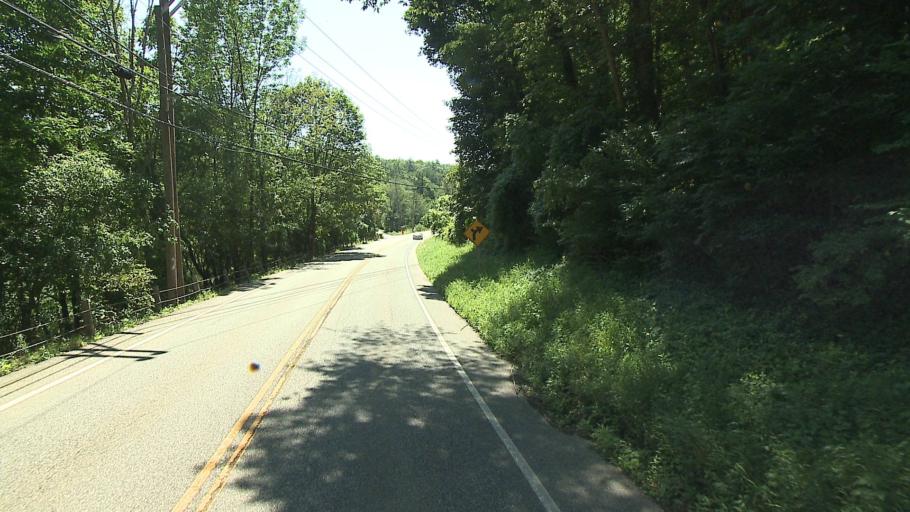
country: US
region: Connecticut
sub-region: Litchfield County
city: Kent
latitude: 41.8744
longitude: -73.4663
